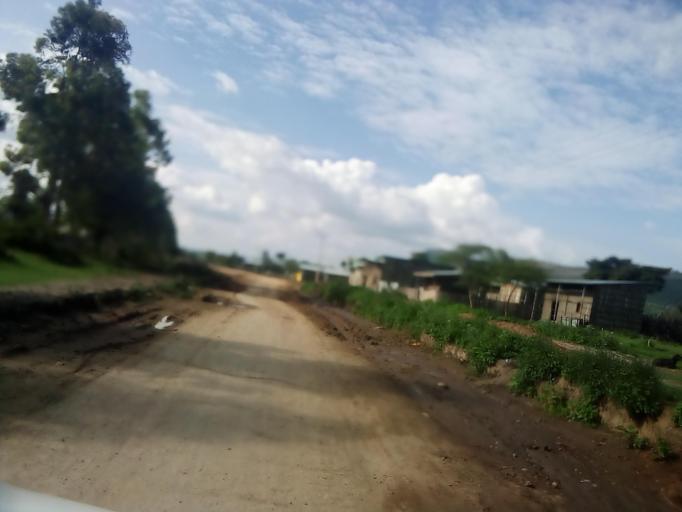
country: ET
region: Southern Nations, Nationalities, and People's Region
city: K'olito
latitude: 7.6078
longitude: 38.0660
